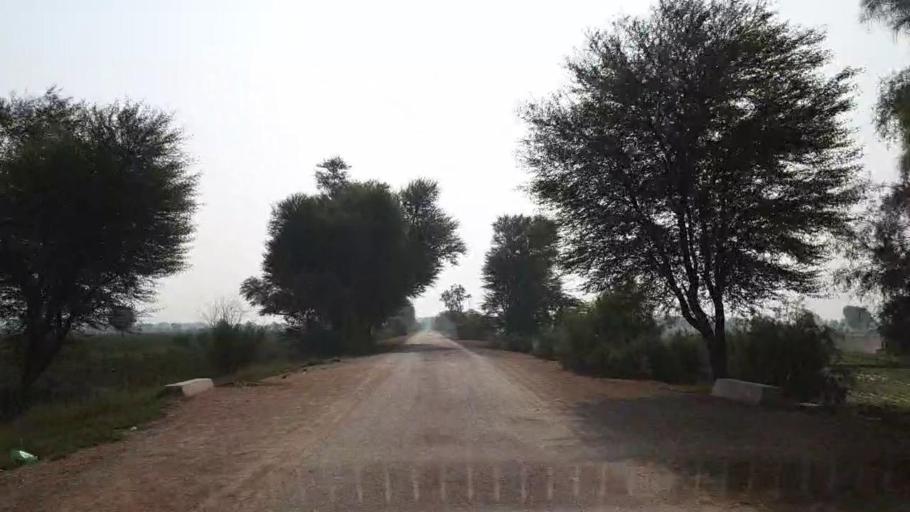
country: PK
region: Sindh
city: Sehwan
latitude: 26.4724
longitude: 67.7747
